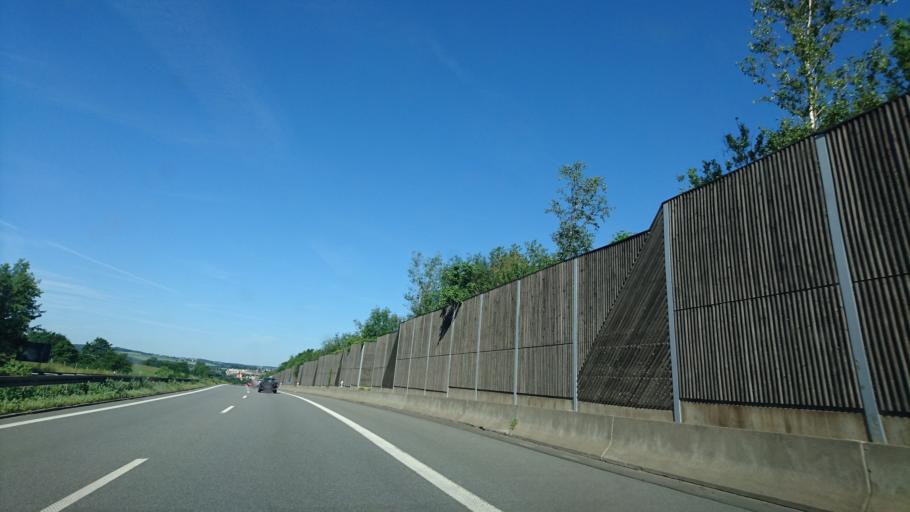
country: DE
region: Saxony
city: Wilkau-Hasslau
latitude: 50.6766
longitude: 12.5440
